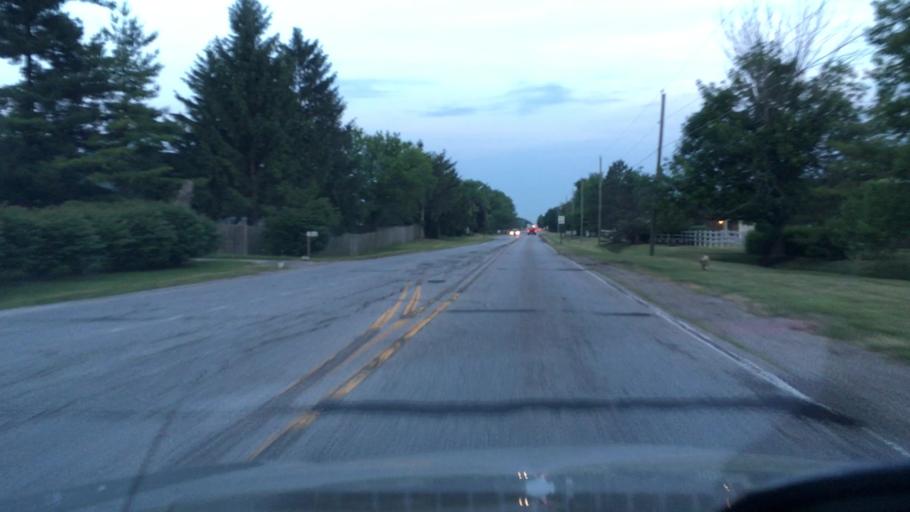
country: US
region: Indiana
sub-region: Marion County
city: Lawrence
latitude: 39.8907
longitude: -86.0336
